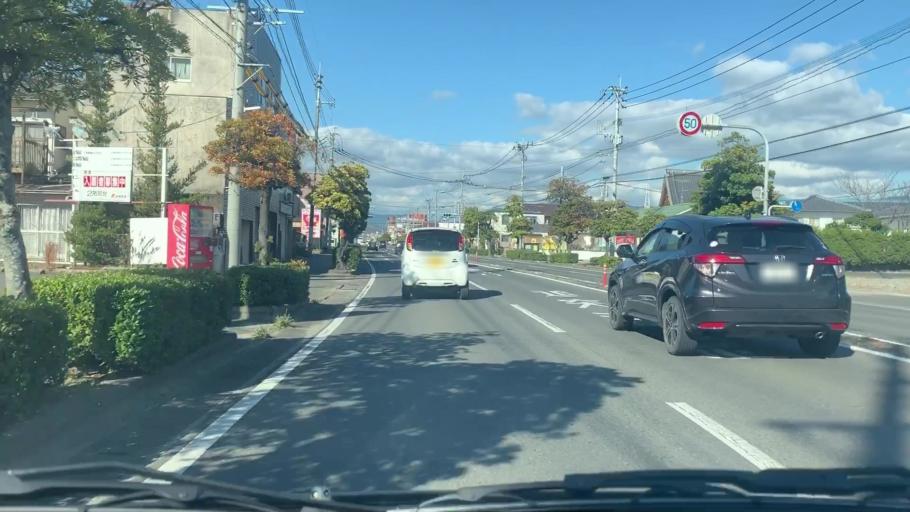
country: JP
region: Saga Prefecture
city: Saga-shi
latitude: 33.2836
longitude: 130.2916
